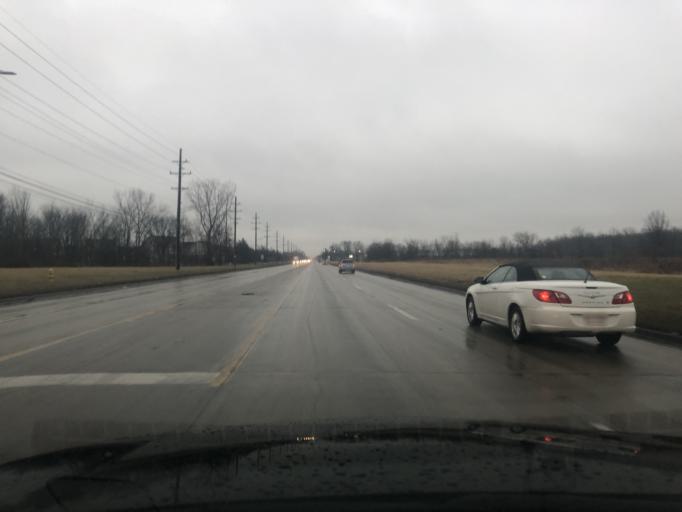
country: US
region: Michigan
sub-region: Wayne County
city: Inkster
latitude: 42.2676
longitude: -83.3412
